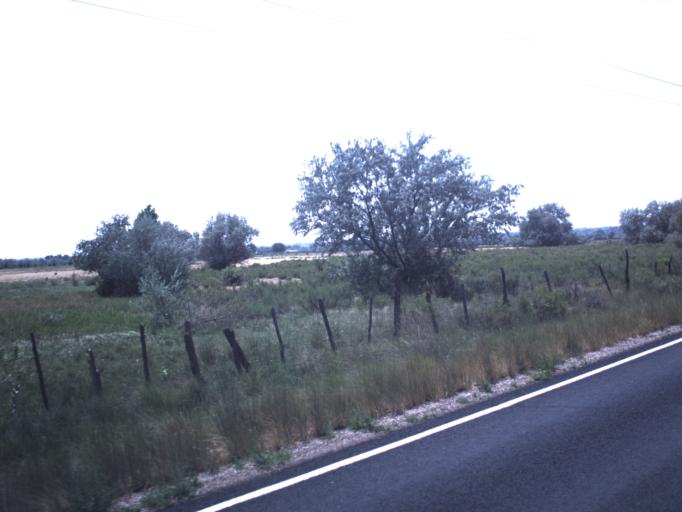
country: US
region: Utah
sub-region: Duchesne County
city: Roosevelt
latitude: 40.4037
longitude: -109.8315
